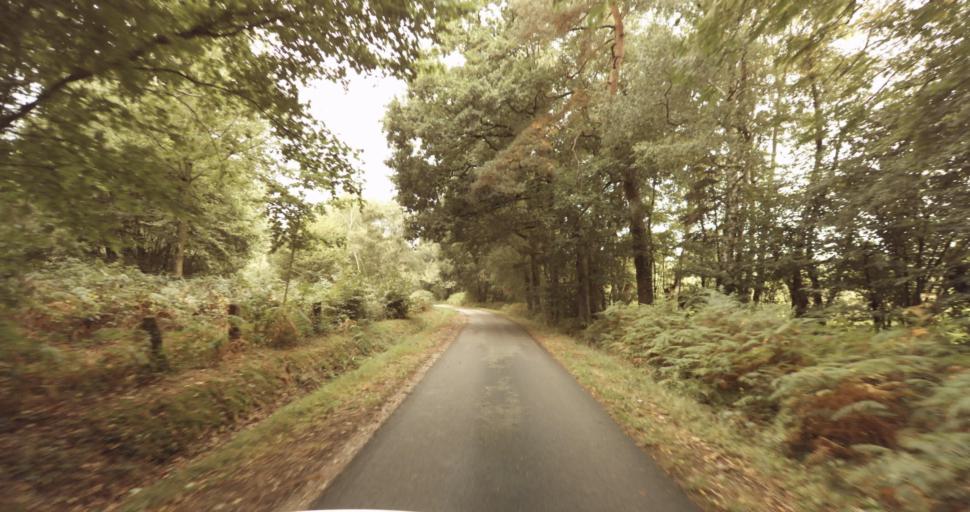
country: FR
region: Lower Normandy
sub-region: Departement du Calvados
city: Livarot
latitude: 48.9394
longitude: 0.0869
